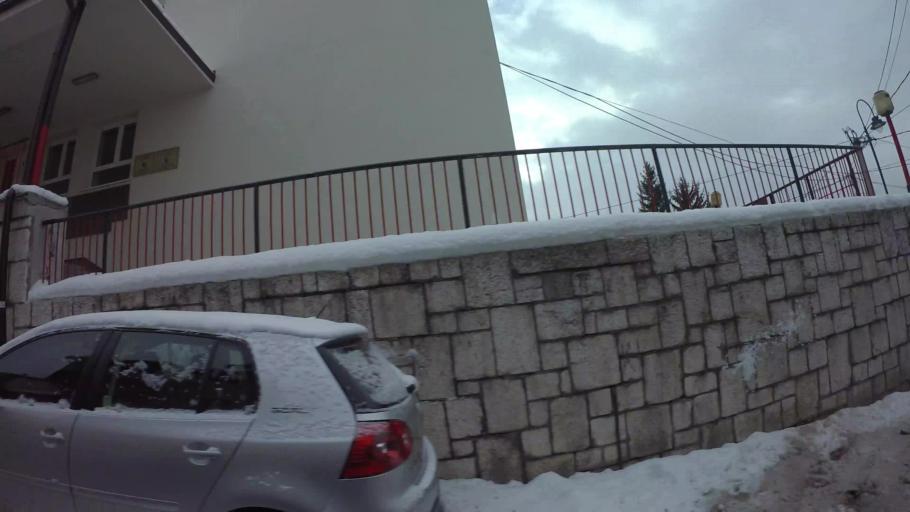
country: BA
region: Federation of Bosnia and Herzegovina
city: Kobilja Glava
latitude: 43.8624
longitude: 18.4426
